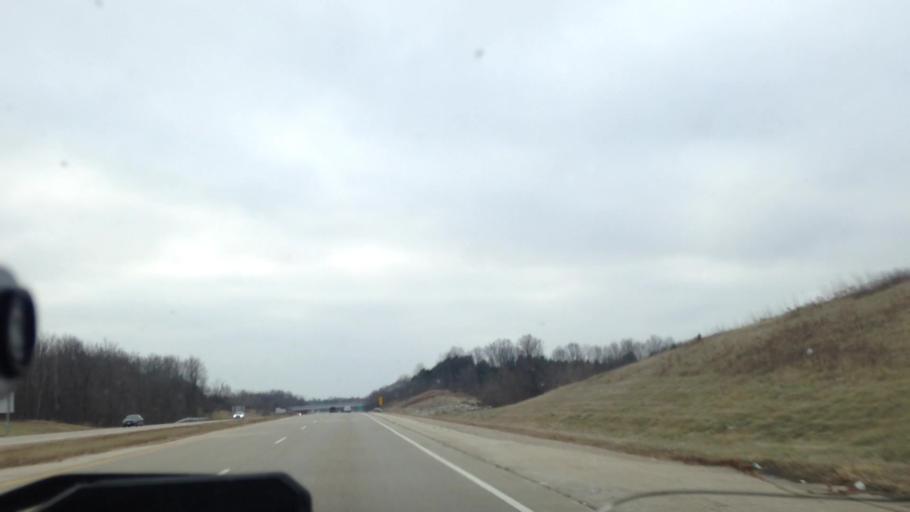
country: US
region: Wisconsin
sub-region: Washington County
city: West Bend
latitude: 43.3833
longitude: -88.1930
